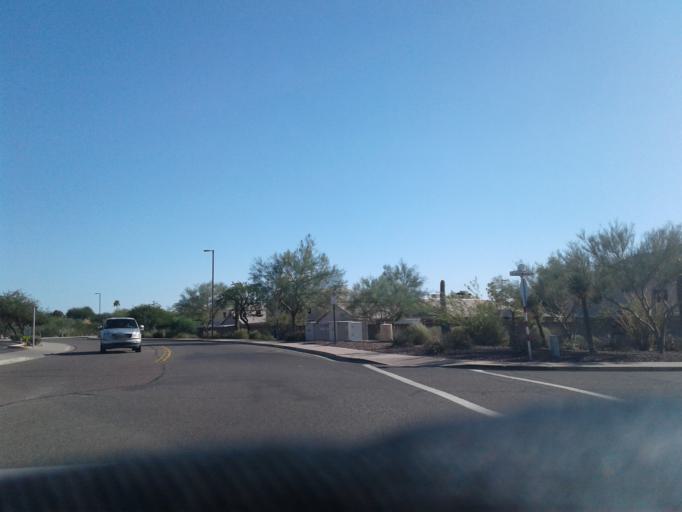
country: US
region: Arizona
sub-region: Maricopa County
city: Cave Creek
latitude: 33.6927
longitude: -112.0363
